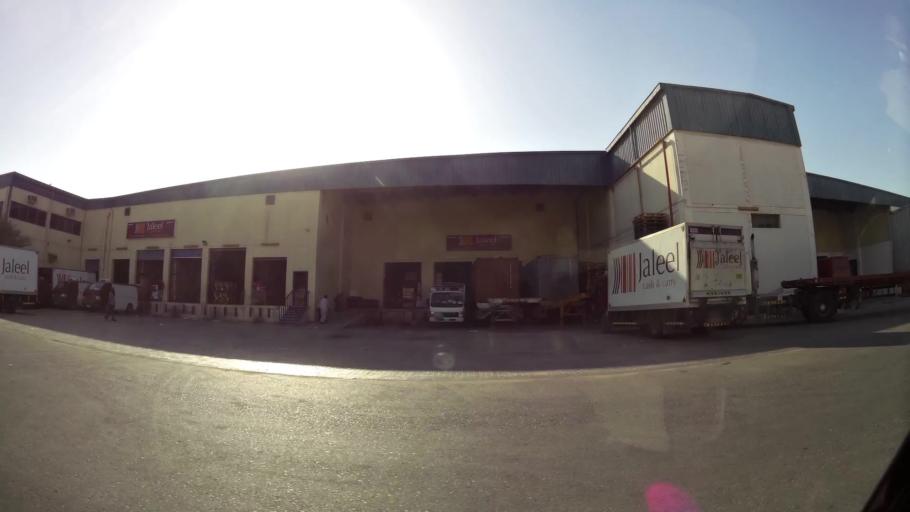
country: AE
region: Dubai
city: Dubai
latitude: 25.1201
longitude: 55.2394
